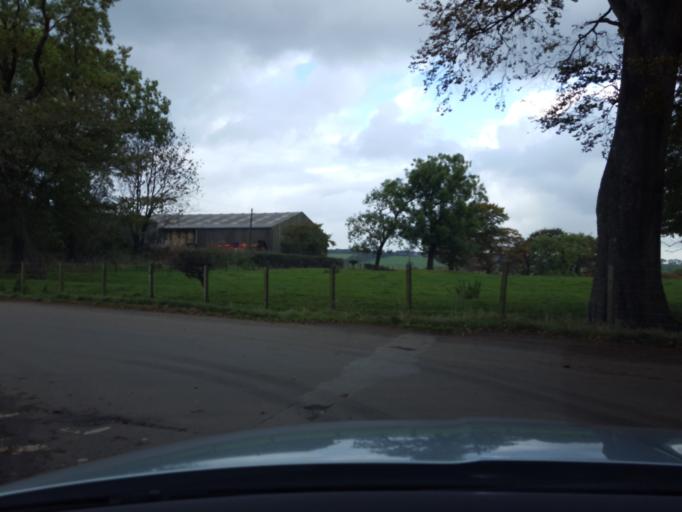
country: GB
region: Scotland
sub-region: West Lothian
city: Bathgate
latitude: 55.9137
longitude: -3.5924
